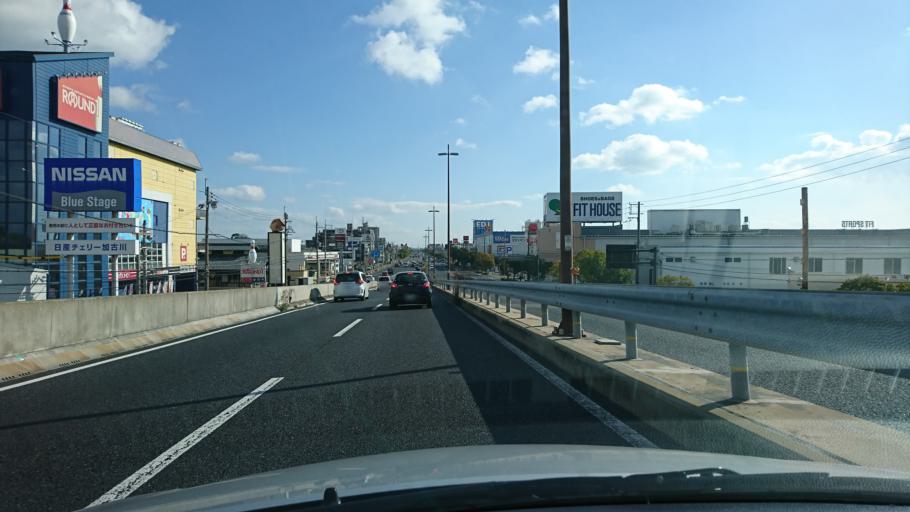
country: JP
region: Hyogo
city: Kakogawacho-honmachi
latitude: 34.7471
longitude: 134.8360
